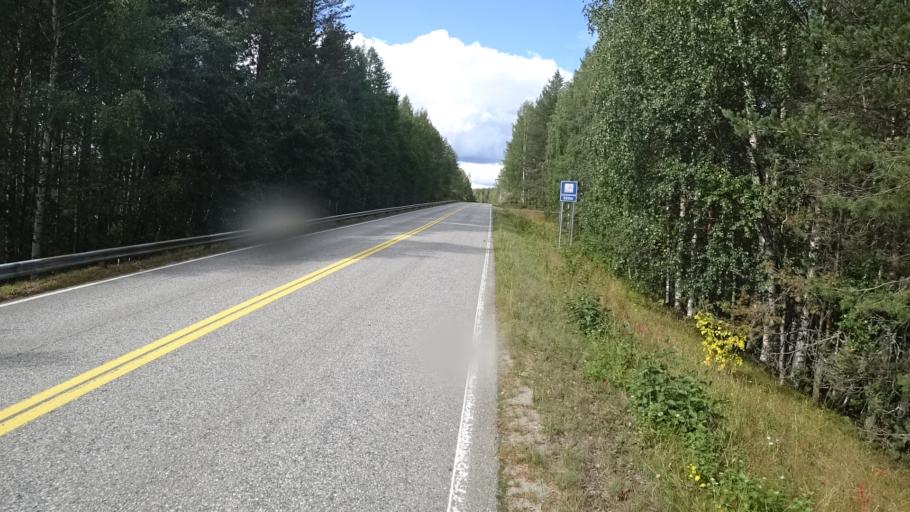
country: FI
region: North Karelia
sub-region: Joensuu
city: Ilomantsi
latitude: 62.6187
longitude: 31.2030
